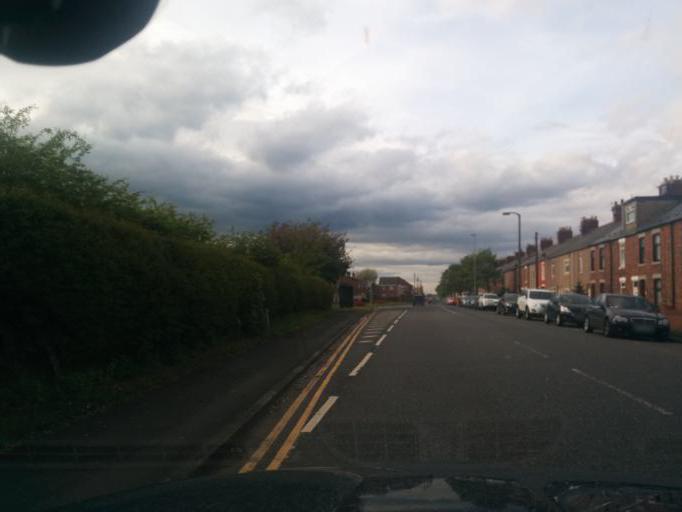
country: GB
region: England
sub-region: Northumberland
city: Ashington
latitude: 55.1595
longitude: -1.5761
